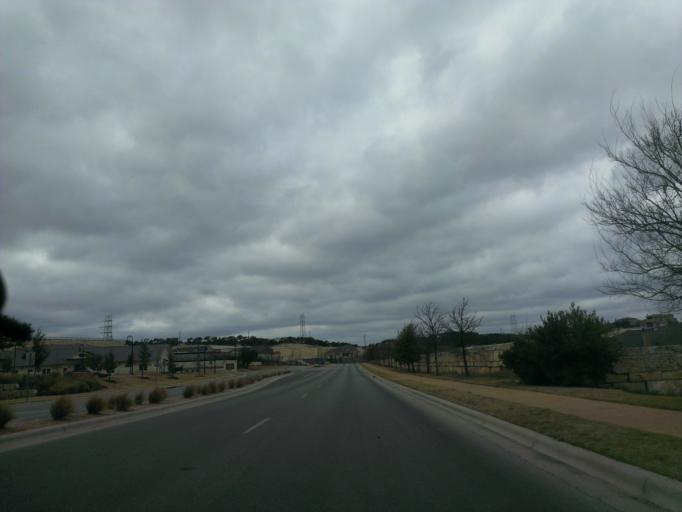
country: US
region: Texas
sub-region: Travis County
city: The Hills
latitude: 30.3506
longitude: -98.0106
